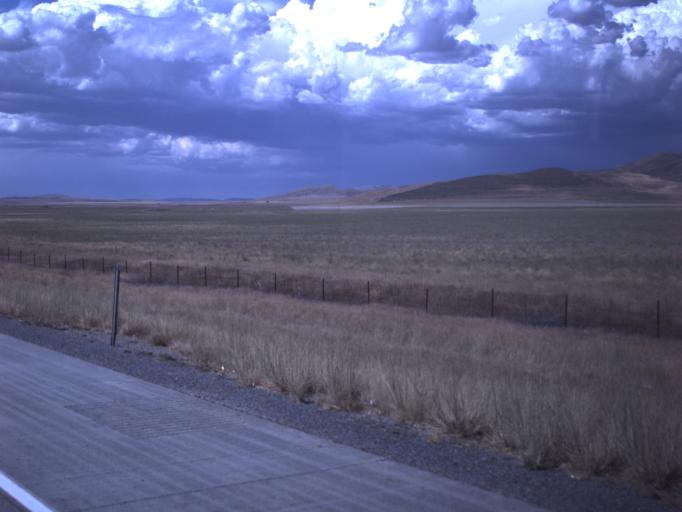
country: US
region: Utah
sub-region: Box Elder County
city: Garland
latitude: 41.8304
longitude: -112.4276
